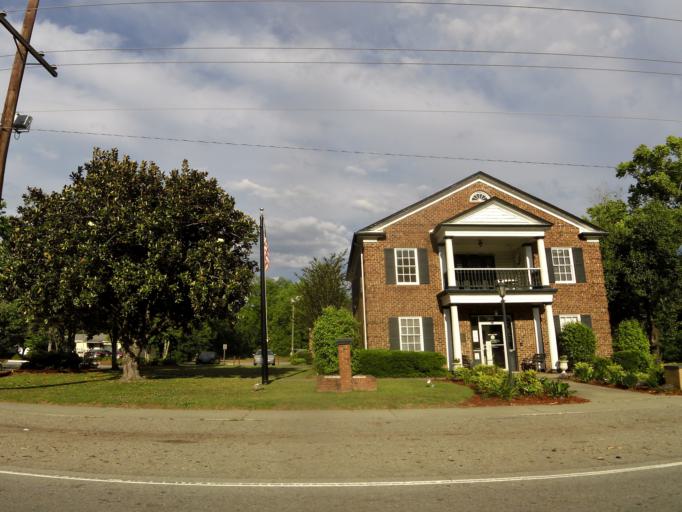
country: US
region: South Carolina
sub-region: Hampton County
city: Estill
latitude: 32.7510
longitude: -81.2413
